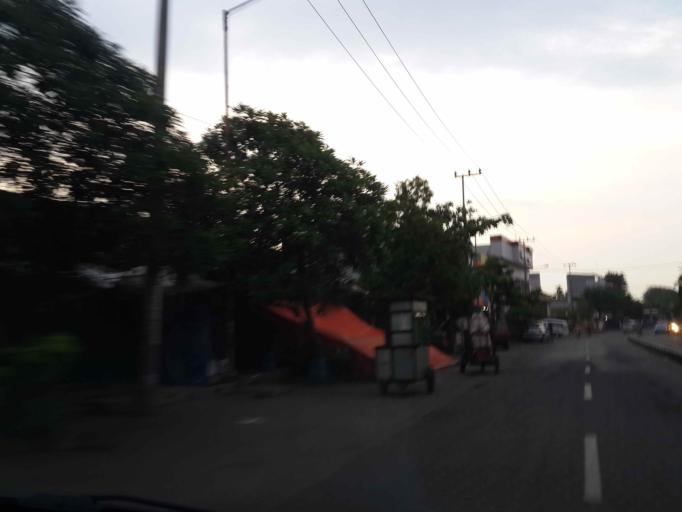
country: ID
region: East Java
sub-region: Kota Surabaya
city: Surabaya
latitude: -7.2550
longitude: 112.7279
